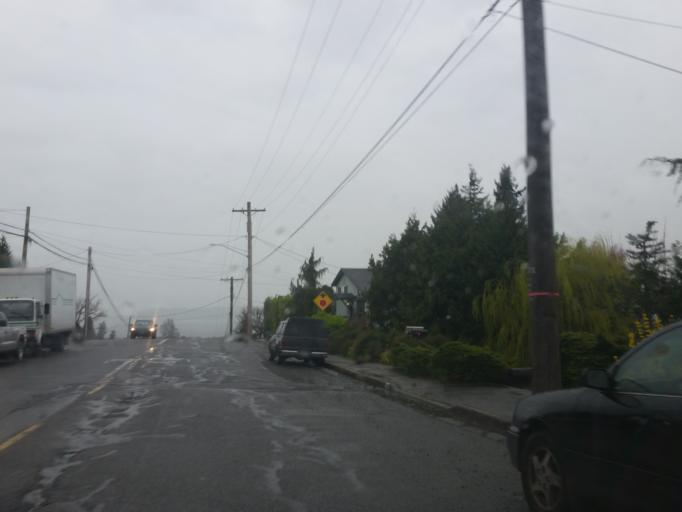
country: US
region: Washington
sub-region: Snohomish County
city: Edmonds
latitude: 47.8074
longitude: -122.3700
